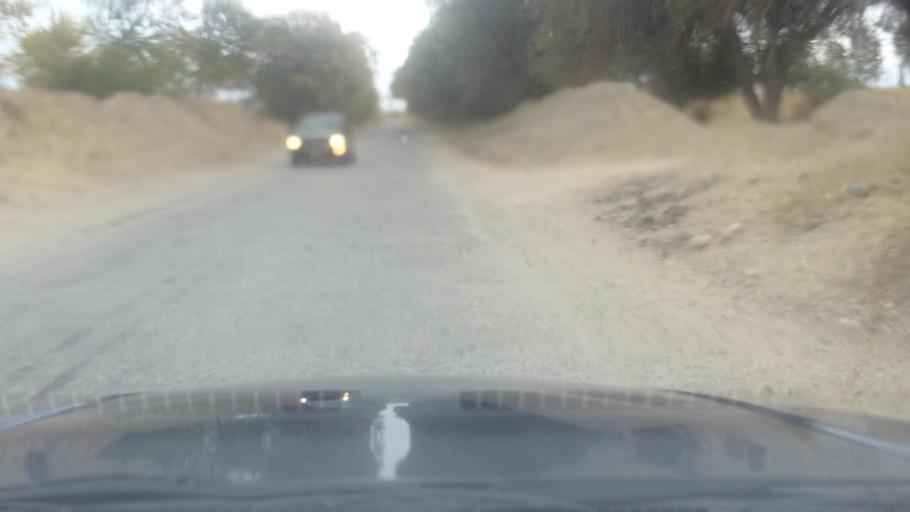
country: KG
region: Ysyk-Koel
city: Balykchy
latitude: 42.3025
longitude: 76.4809
